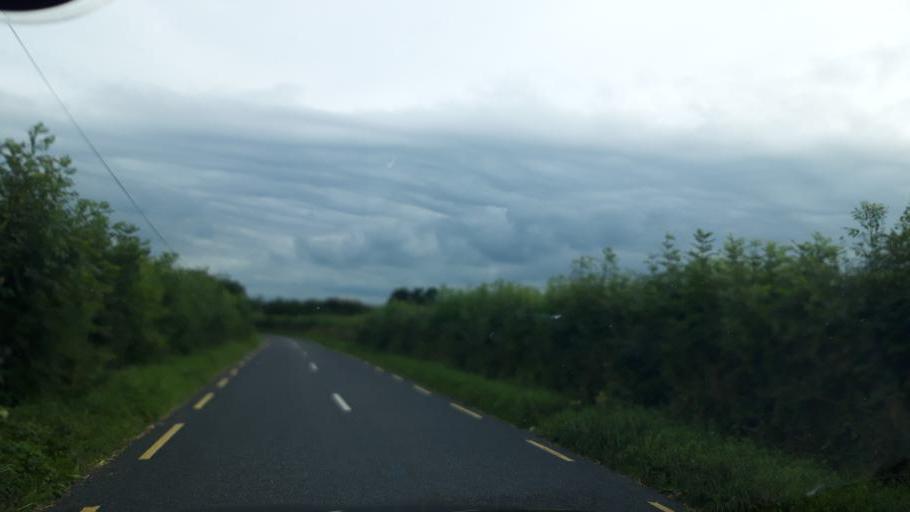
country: IE
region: Leinster
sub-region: Kilkenny
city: Ballyragget
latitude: 52.7529
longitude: -7.3921
